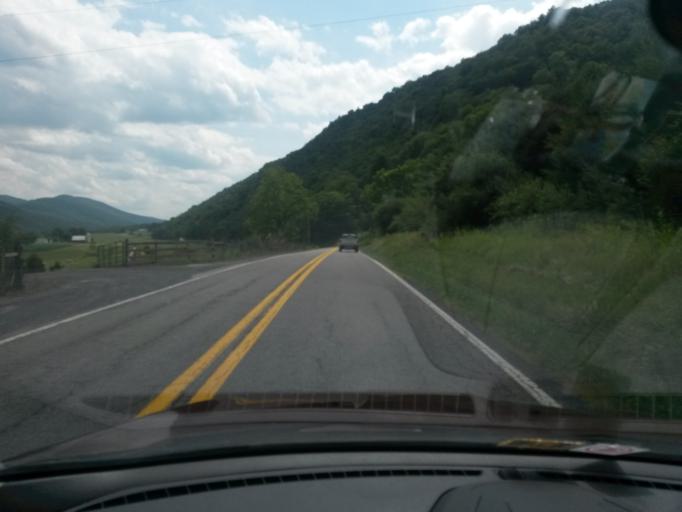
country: US
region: West Virginia
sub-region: Pendleton County
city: Franklin
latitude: 38.5868
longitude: -79.4109
